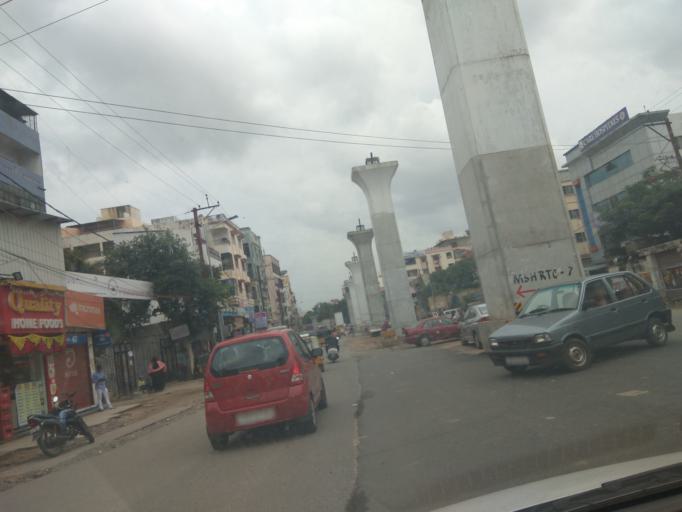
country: IN
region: Telangana
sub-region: Hyderabad
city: Malkajgiri
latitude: 17.4157
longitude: 78.4984
